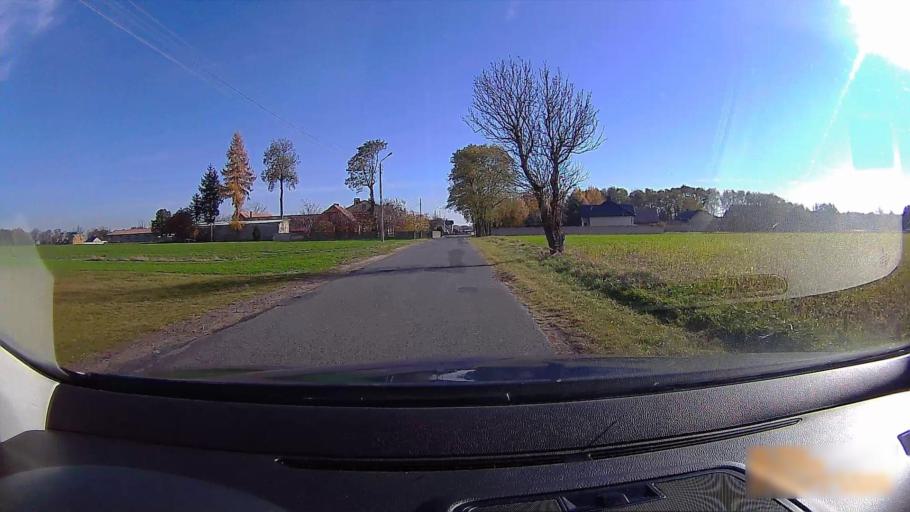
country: PL
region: Greater Poland Voivodeship
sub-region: Powiat ostrzeszowski
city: Doruchow
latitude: 51.3924
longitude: 18.0515
